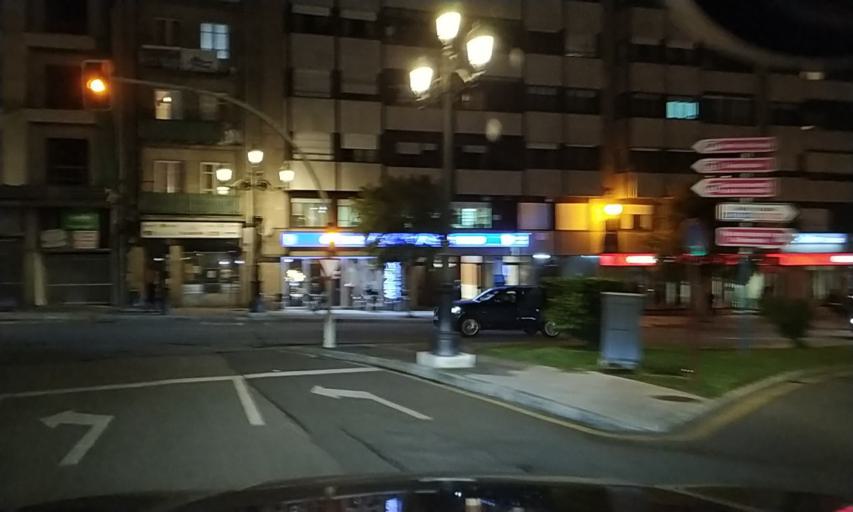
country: ES
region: Galicia
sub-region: Provincia de Ourense
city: Ourense
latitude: 42.3430
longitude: -7.8679
